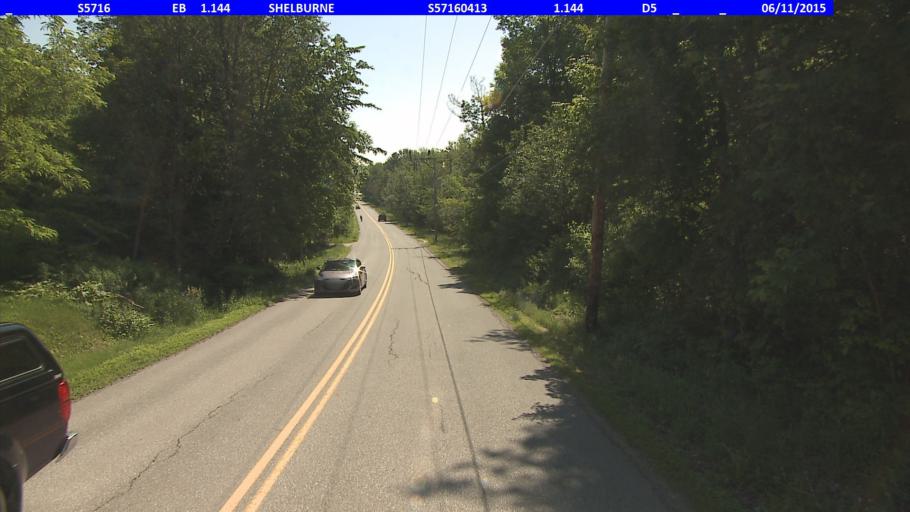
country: US
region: Vermont
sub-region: Chittenden County
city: Hinesburg
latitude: 44.3713
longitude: -73.1896
